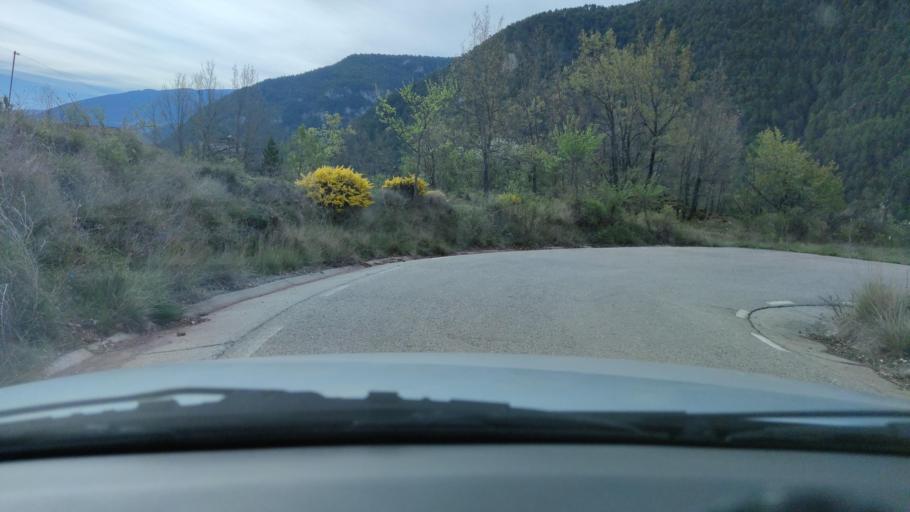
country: ES
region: Catalonia
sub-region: Provincia de Lleida
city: la Seu d'Urgell
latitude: 42.2411
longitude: 1.4354
